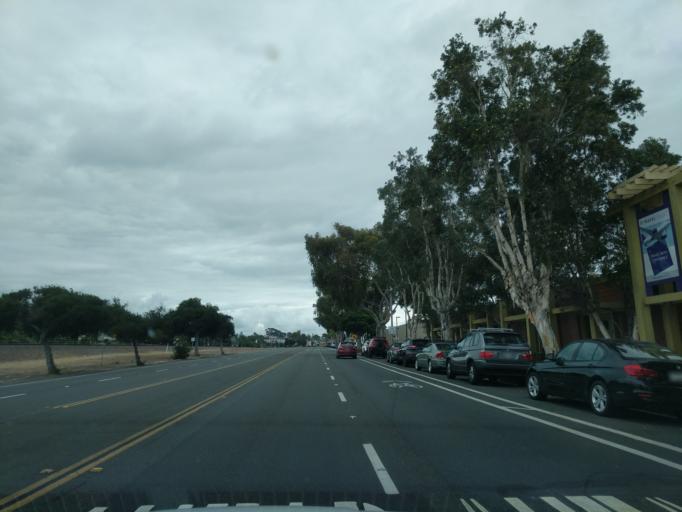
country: US
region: California
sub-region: San Diego County
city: Encinitas
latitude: 33.0562
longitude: -117.2979
